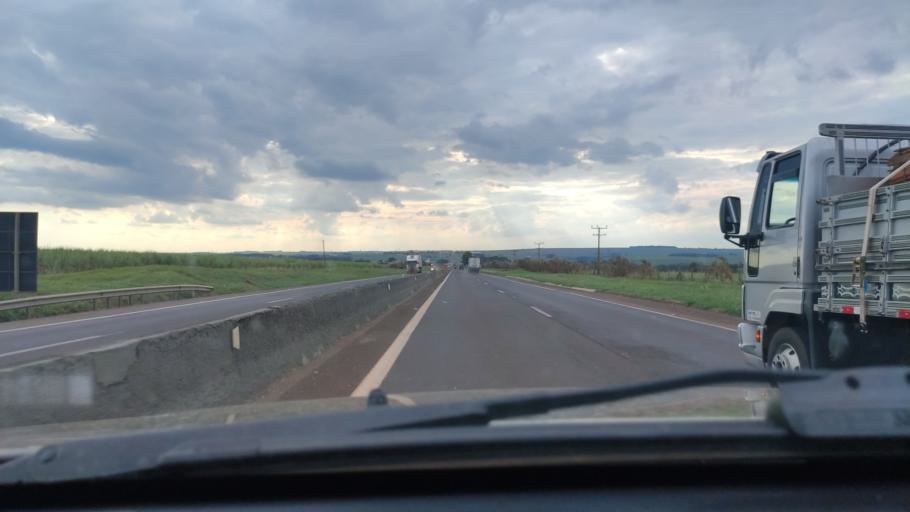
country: BR
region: Sao Paulo
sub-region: Palmital
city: Palmital
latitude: -22.7217
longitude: -50.2394
